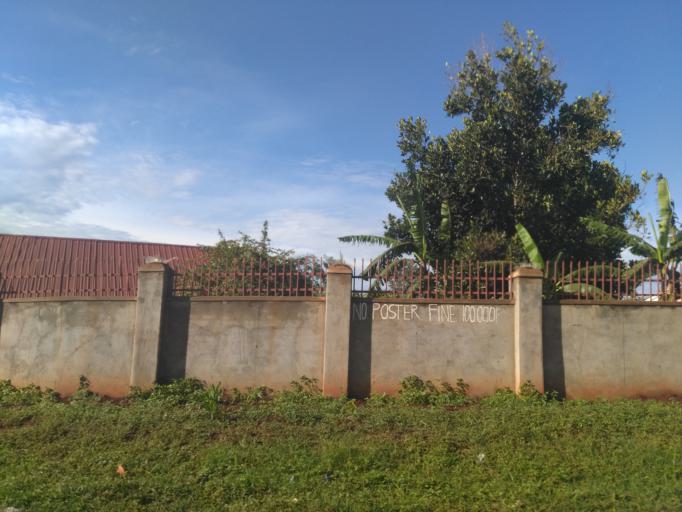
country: UG
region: Eastern Region
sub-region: Jinja District
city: Jinja
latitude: 0.4490
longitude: 33.1959
